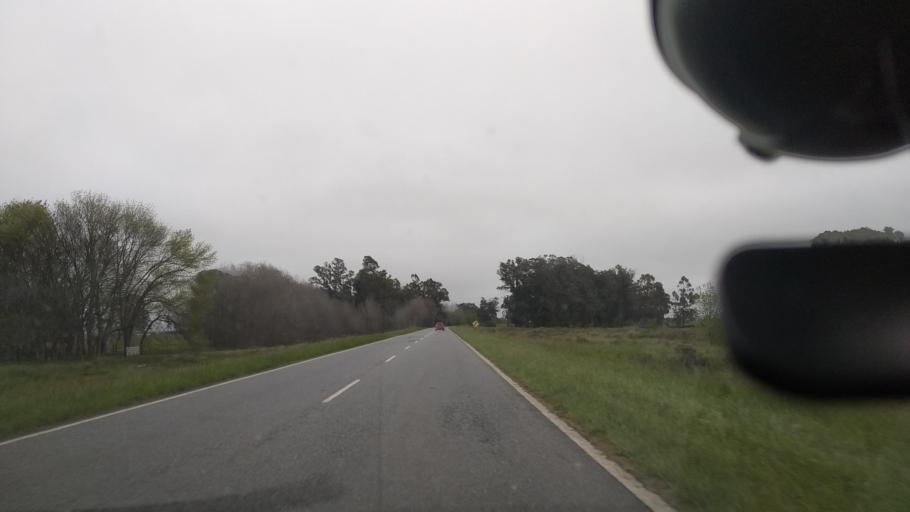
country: AR
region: Buenos Aires
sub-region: Partido de Magdalena
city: Magdalena
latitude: -35.2654
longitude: -57.6228
